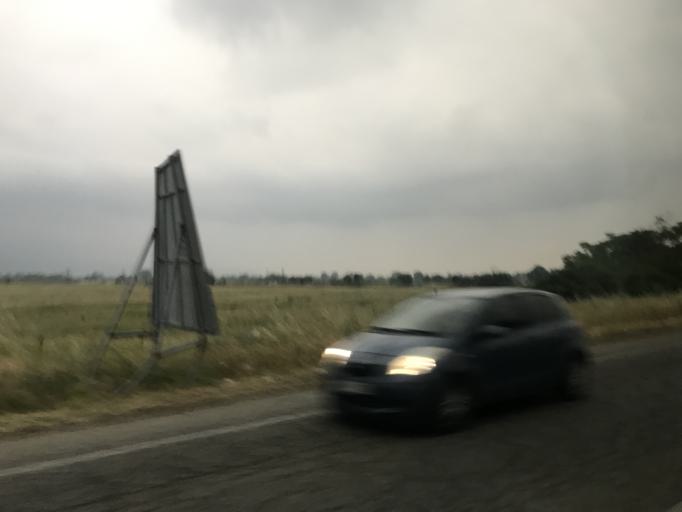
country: GR
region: East Macedonia and Thrace
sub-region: Nomos Xanthis
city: Peteinos
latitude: 41.1140
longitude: 24.9200
